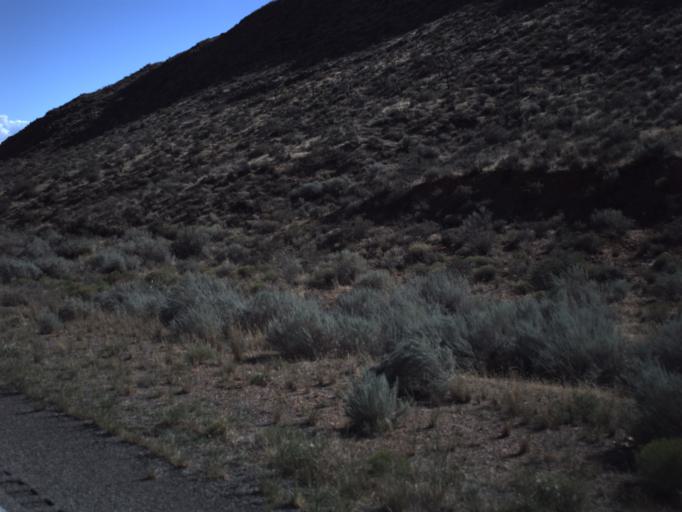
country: US
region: Utah
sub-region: Washington County
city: Toquerville
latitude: 37.2723
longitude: -113.2967
